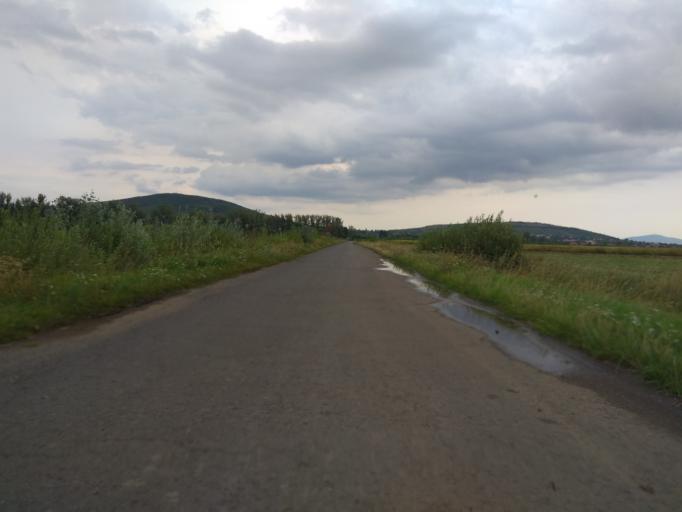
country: HU
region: Borsod-Abauj-Zemplen
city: Bekecs
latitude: 48.1571
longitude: 21.1313
